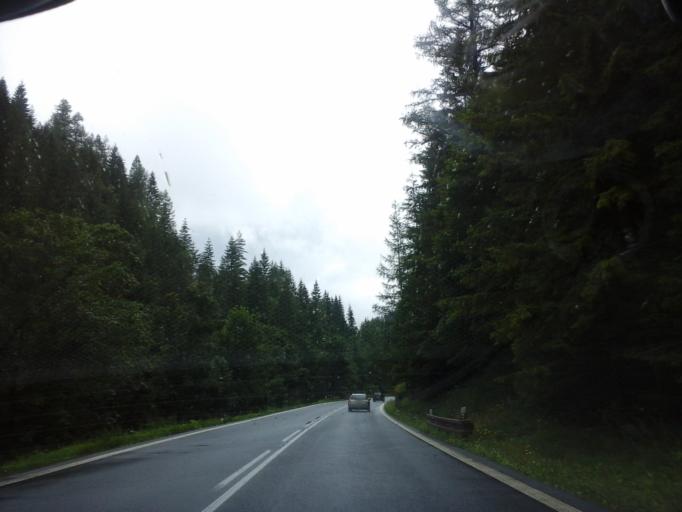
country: SK
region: Kosicky
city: Dobsina
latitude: 48.8770
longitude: 20.2618
